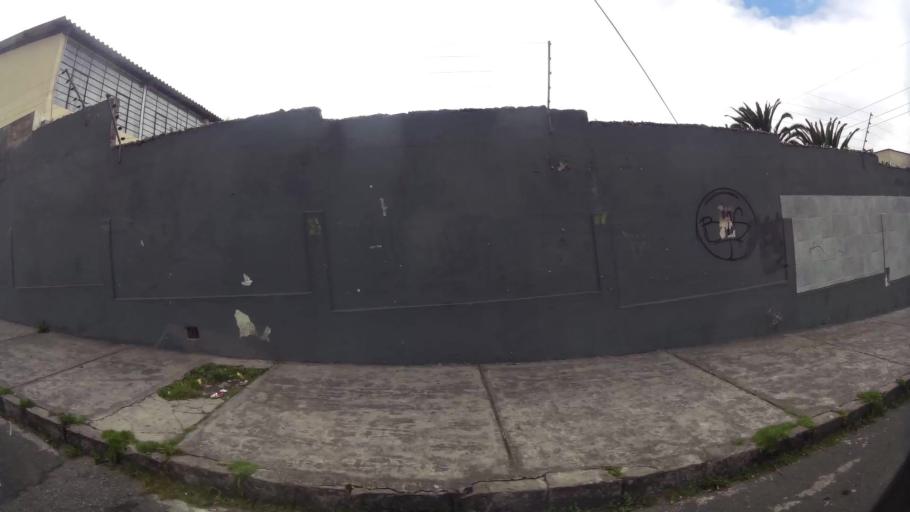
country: EC
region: Pichincha
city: Quito
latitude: -0.1395
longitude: -78.4970
